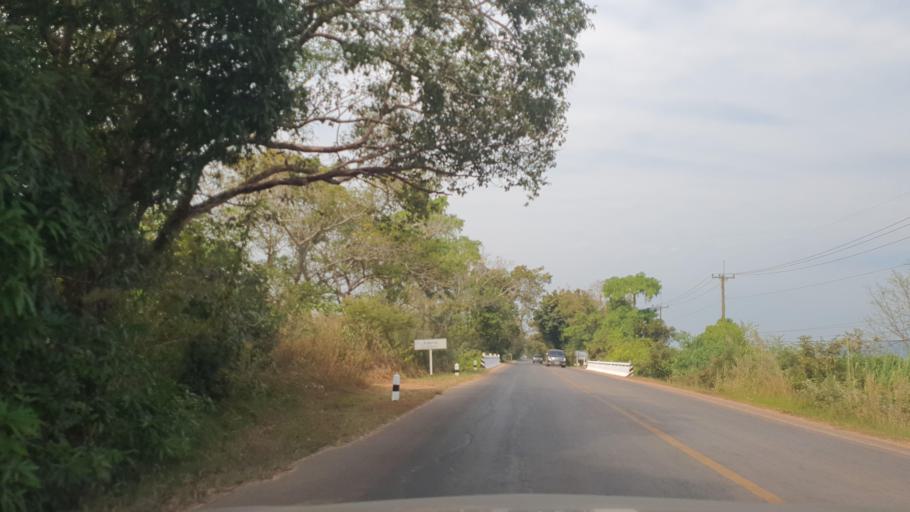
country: TH
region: Changwat Bueng Kan
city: Bung Khla
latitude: 18.2137
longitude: 104.0430
